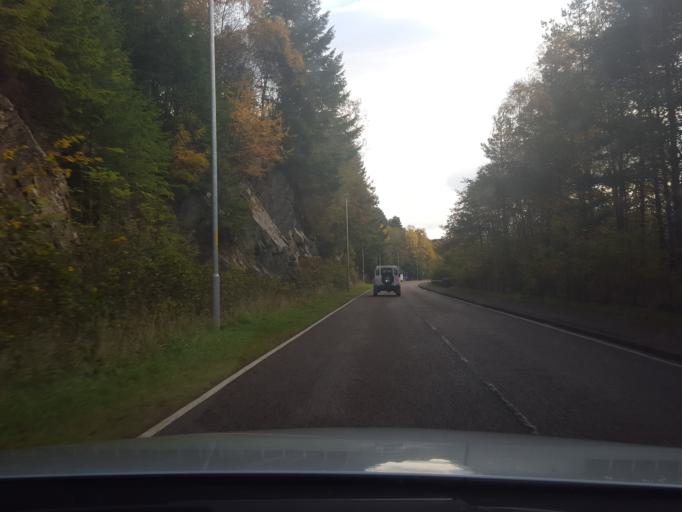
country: GB
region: Scotland
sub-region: Highland
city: Beauly
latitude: 57.2167
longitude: -4.6234
